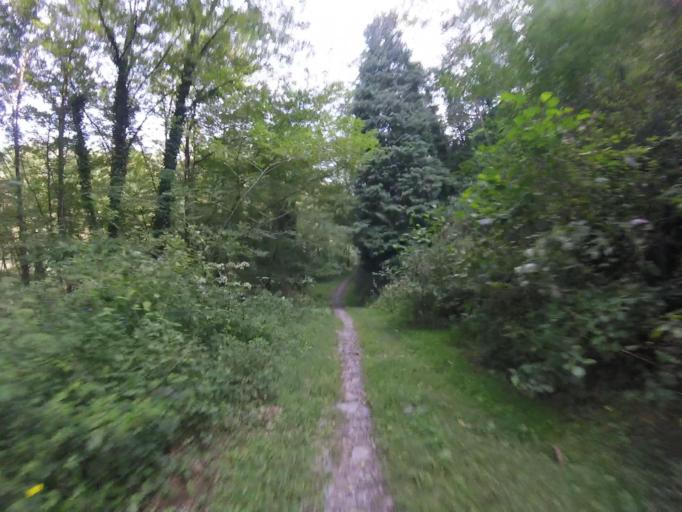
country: ES
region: Navarre
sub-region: Provincia de Navarra
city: Arano
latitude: 43.2306
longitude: -1.9338
